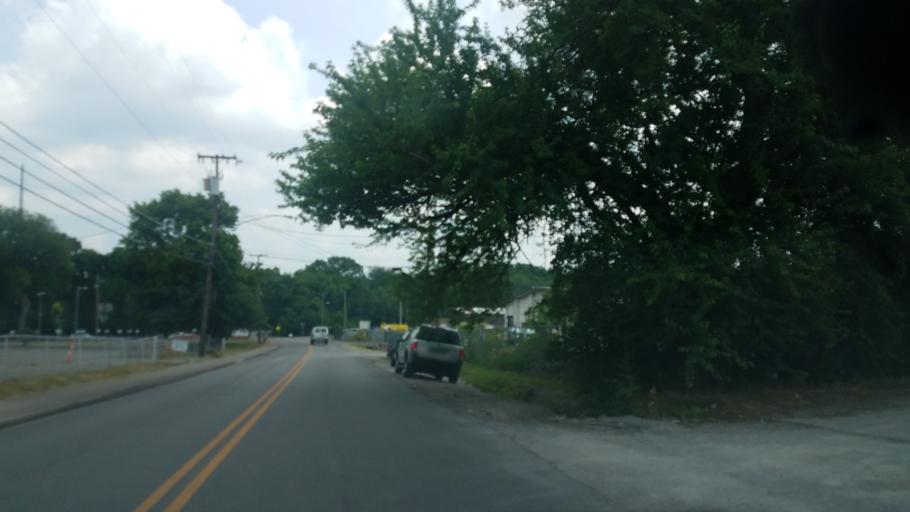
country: US
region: Tennessee
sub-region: Davidson County
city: Oak Hill
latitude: 36.1150
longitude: -86.7422
